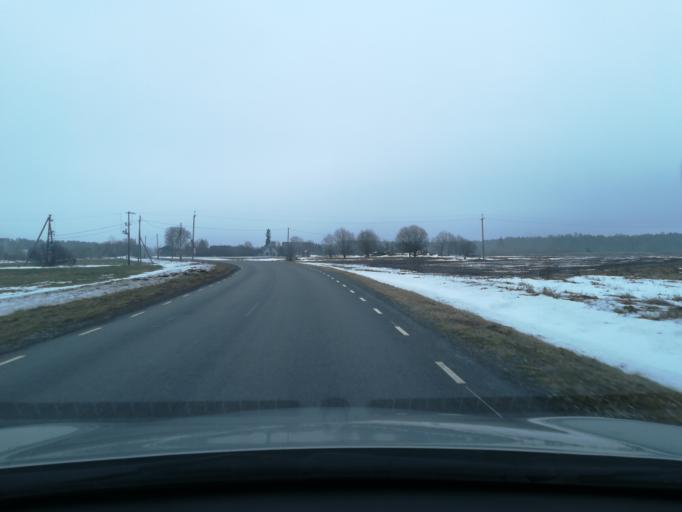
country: EE
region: Harju
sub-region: Kuusalu vald
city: Kuusalu
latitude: 59.4719
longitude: 25.5554
